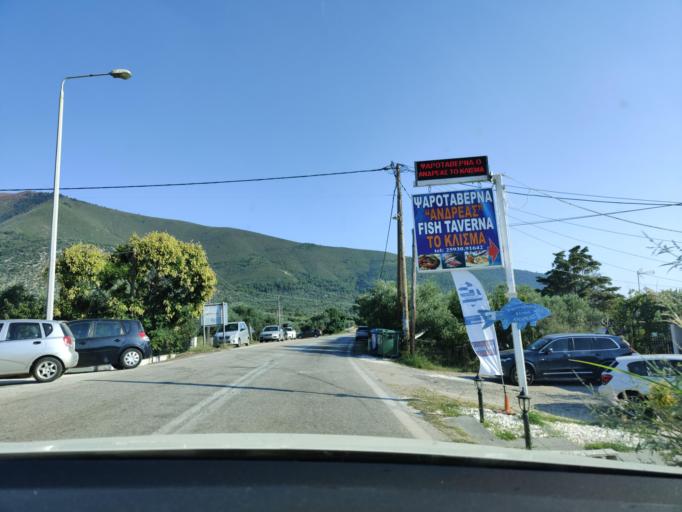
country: GR
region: East Macedonia and Thrace
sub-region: Nomos Kavalas
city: Prinos
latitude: 40.6921
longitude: 24.5263
